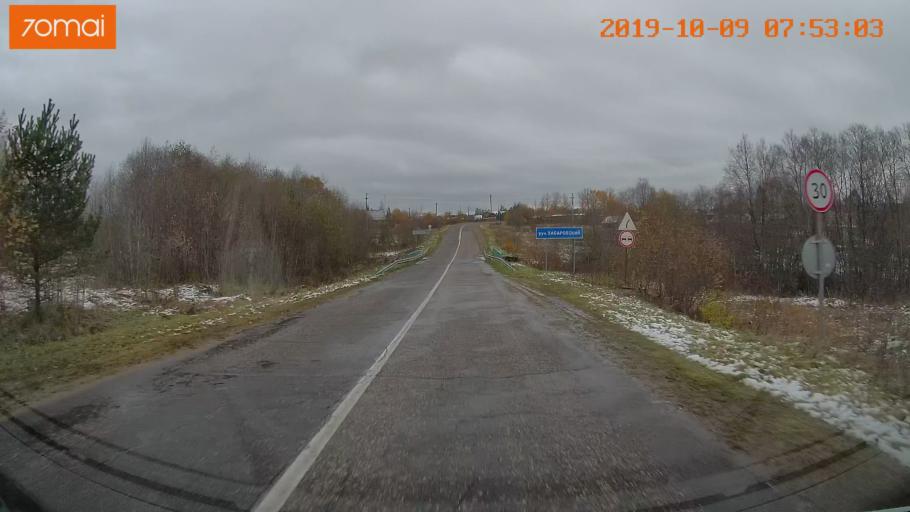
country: RU
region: Jaroslavl
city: Kukoboy
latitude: 58.6959
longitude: 39.8919
